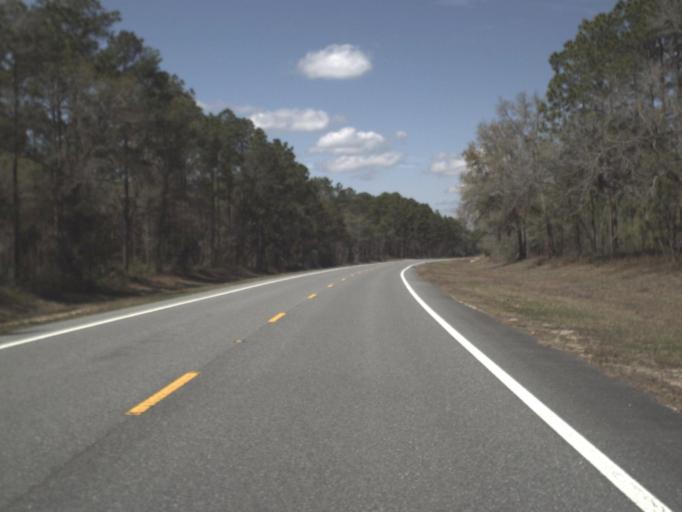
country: US
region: Florida
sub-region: Wakulla County
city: Crawfordville
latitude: 30.2906
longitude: -84.4061
